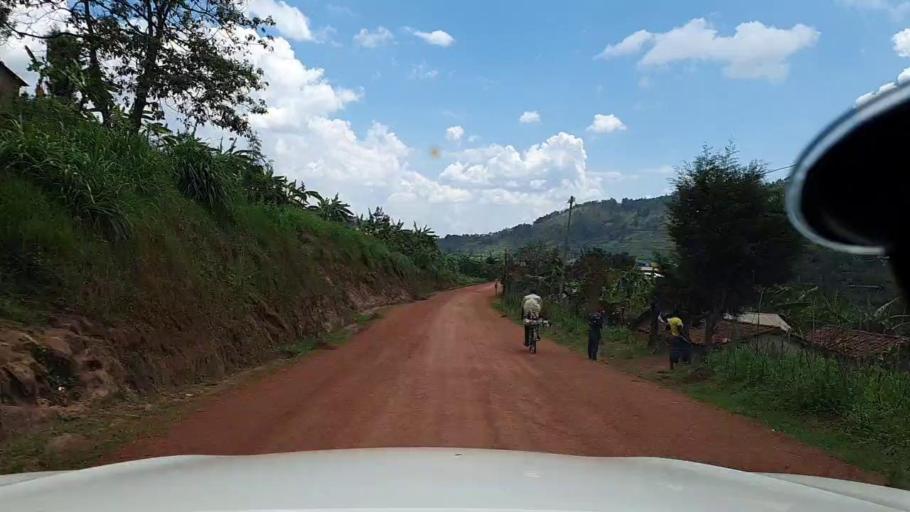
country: RW
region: Kigali
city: Kigali
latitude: -1.7709
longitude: 29.8422
